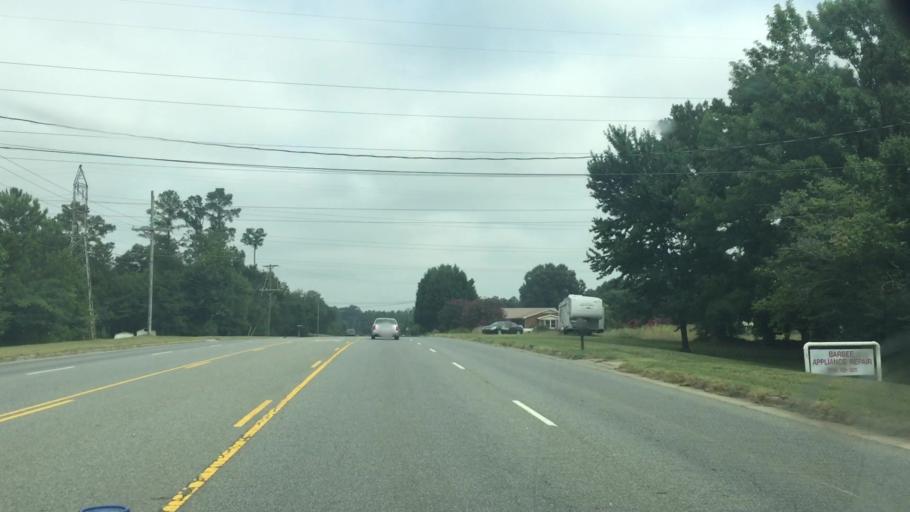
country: US
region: North Carolina
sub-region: Cabarrus County
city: Kannapolis
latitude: 35.4293
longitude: -80.6794
